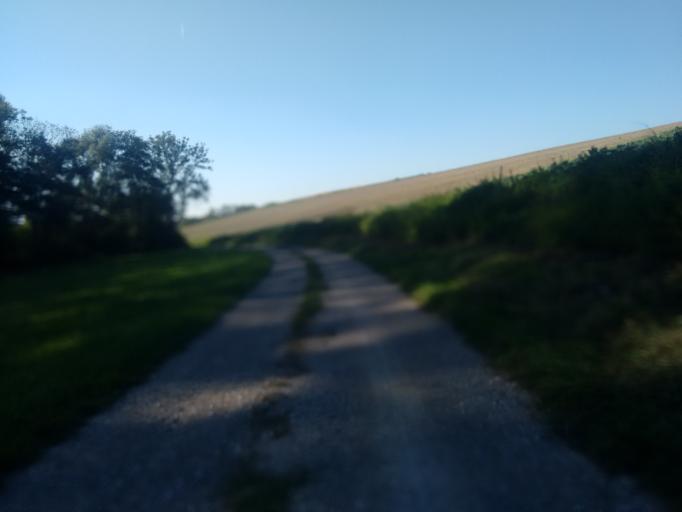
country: AT
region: Upper Austria
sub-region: Wels-Land
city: Buchkirchen
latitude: 48.1958
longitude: 13.9842
